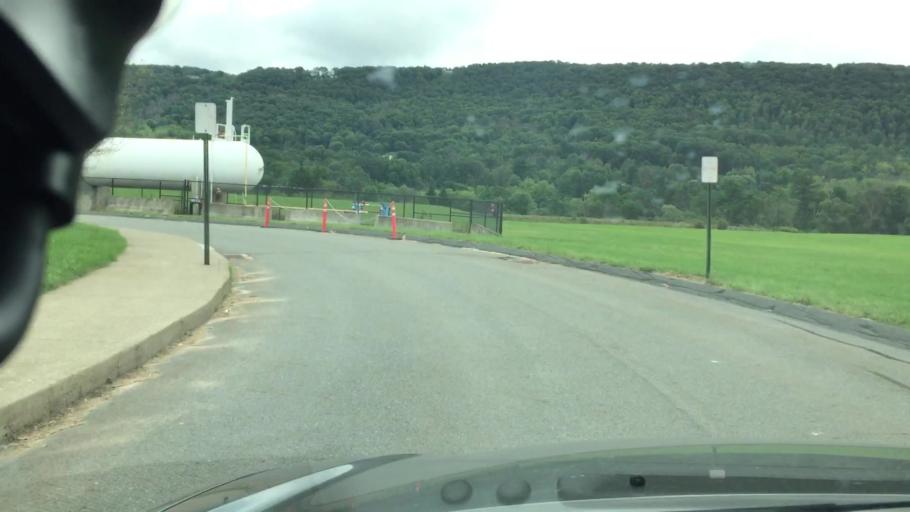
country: US
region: Pennsylvania
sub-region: Luzerne County
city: Harleigh
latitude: 41.0102
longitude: -76.0017
